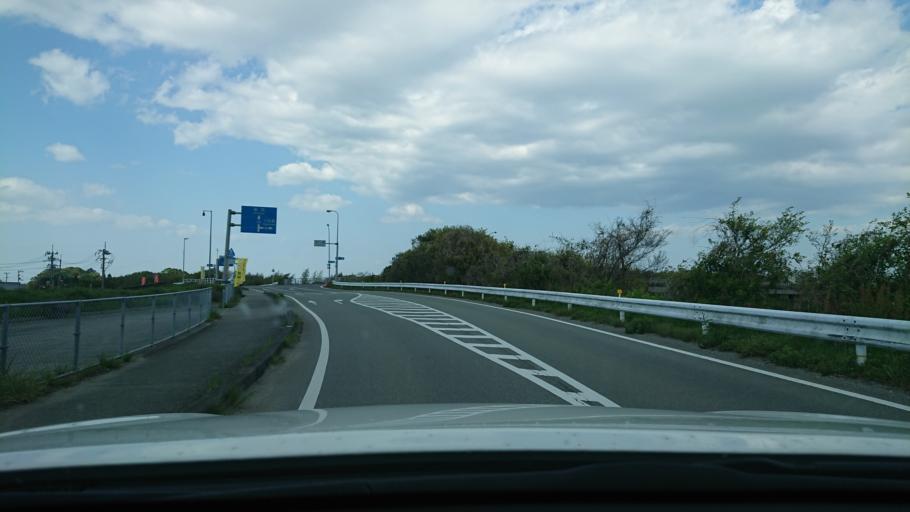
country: JP
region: Tokushima
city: Komatsushimacho
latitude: 33.9944
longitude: 134.5468
